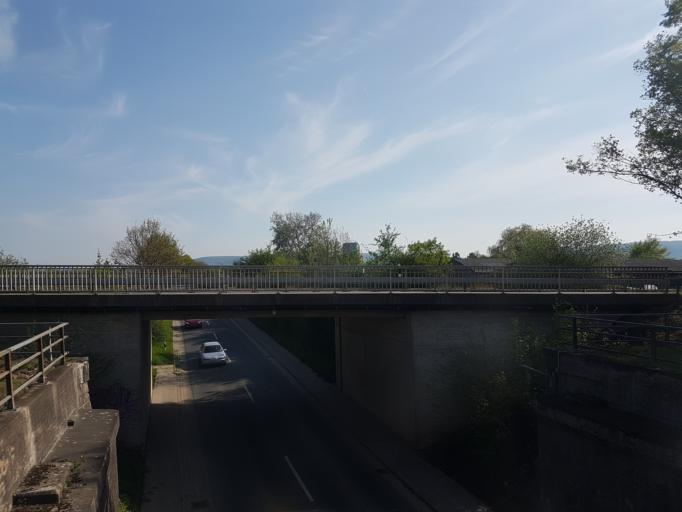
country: DE
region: Lower Saxony
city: Springe
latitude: 52.2118
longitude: 9.6286
